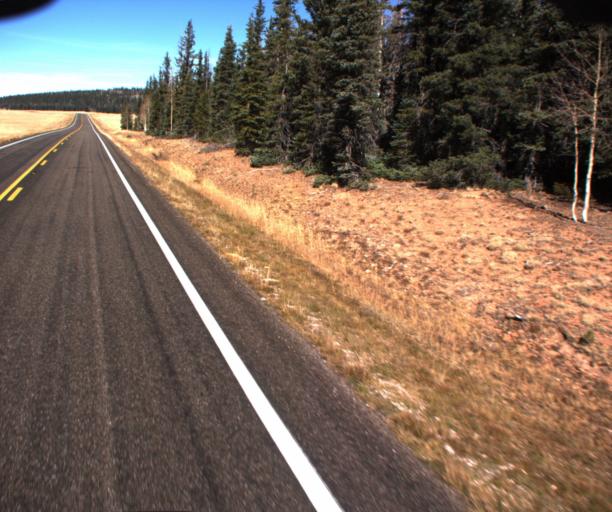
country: US
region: Arizona
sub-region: Coconino County
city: Grand Canyon
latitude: 36.3509
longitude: -112.1180
